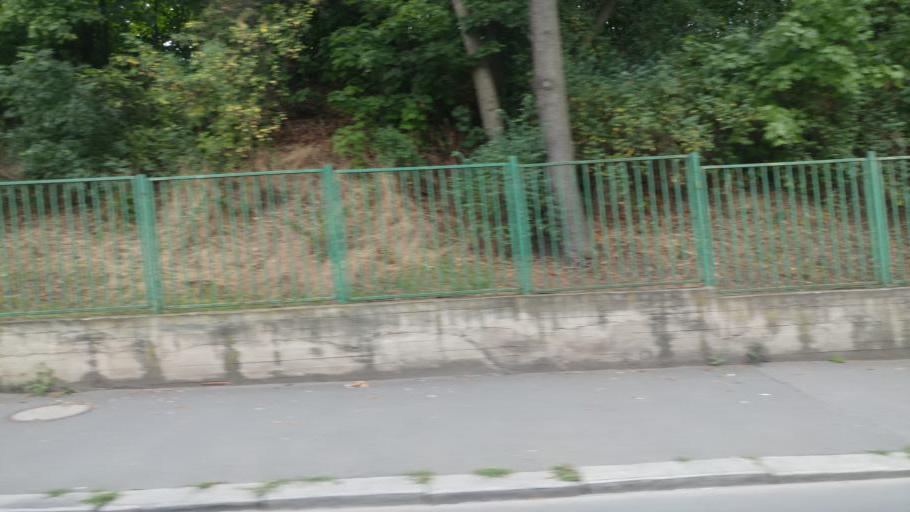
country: CZ
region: Praha
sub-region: Praha 9
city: Vysocany
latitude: 50.0920
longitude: 14.5131
